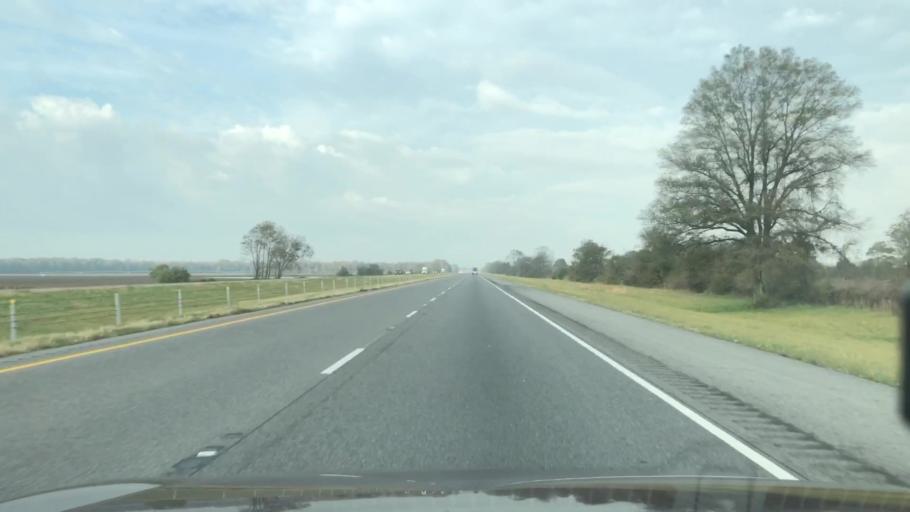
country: US
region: Louisiana
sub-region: Madison Parish
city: Tallulah
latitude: 32.4224
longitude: -91.3390
